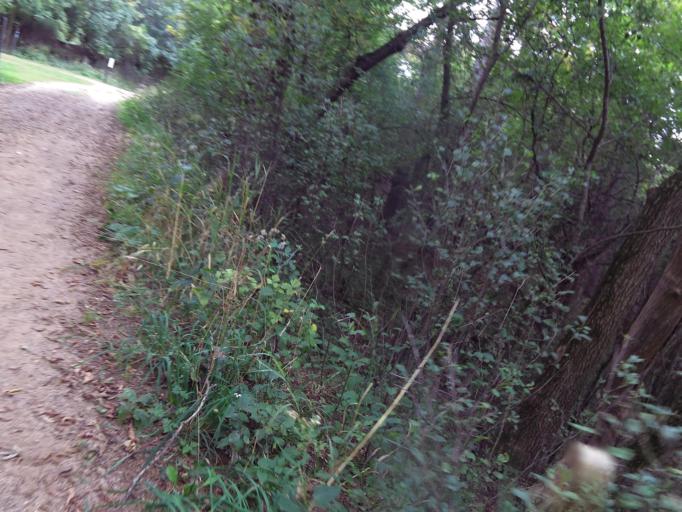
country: US
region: Minnesota
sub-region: Washington County
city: Afton
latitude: 44.8691
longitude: -92.7818
